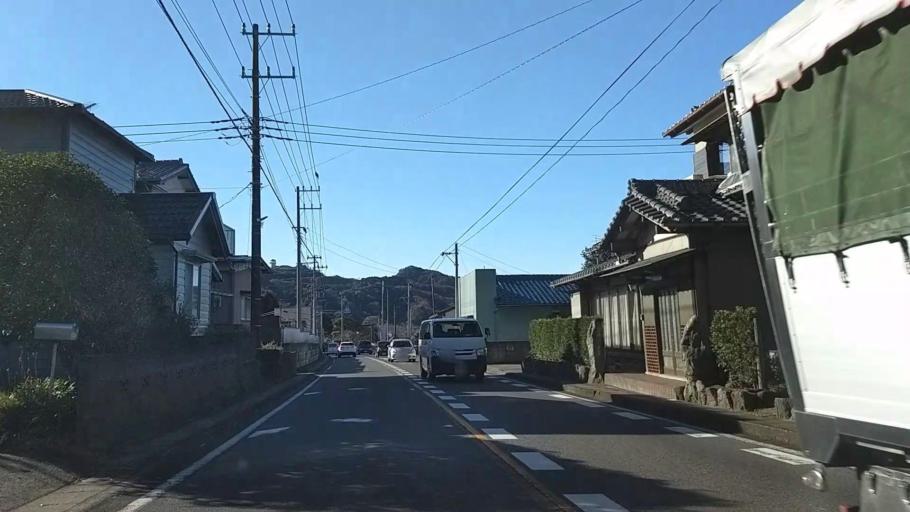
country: JP
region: Chiba
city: Futtsu
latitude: 35.2100
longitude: 139.8468
